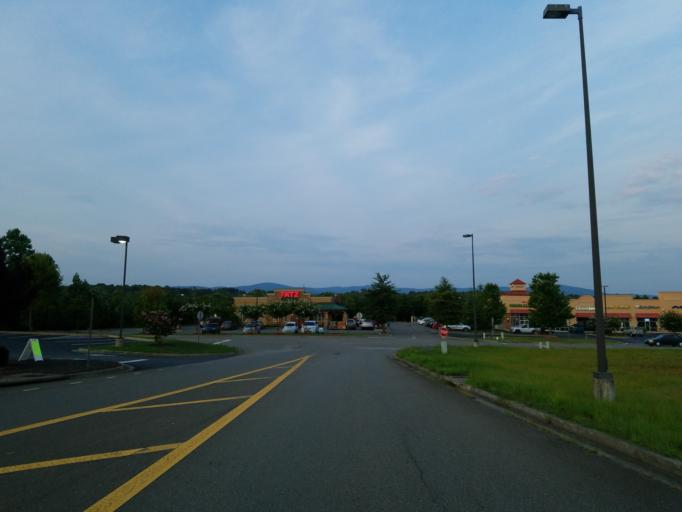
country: US
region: Georgia
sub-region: Pickens County
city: Jasper
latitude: 34.4700
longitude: -84.4600
